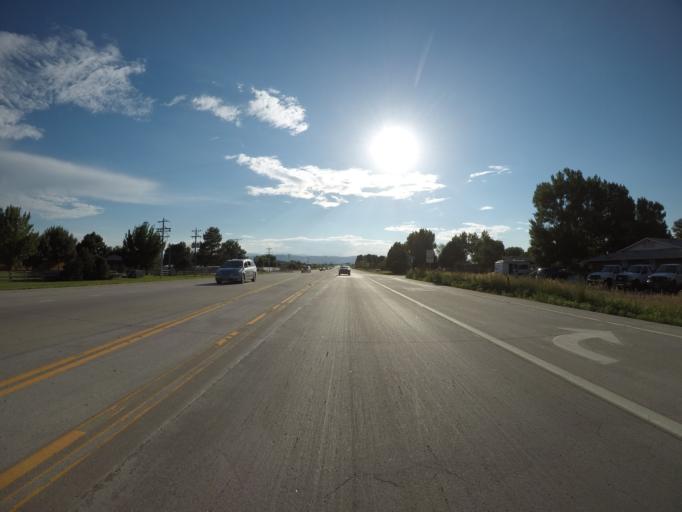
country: US
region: Colorado
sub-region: Larimer County
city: Fort Collins
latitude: 40.5812
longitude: -104.9905
